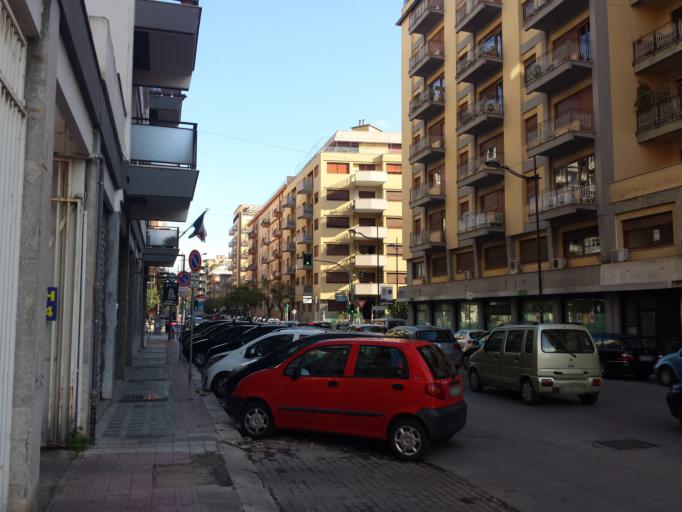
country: IT
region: Sicily
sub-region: Palermo
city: Palermo
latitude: 38.1324
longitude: 13.3469
